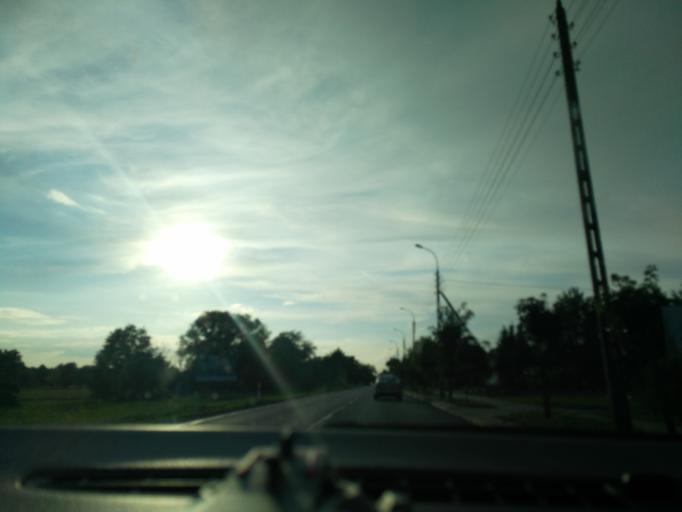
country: PL
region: Lublin Voivodeship
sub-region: Powiat krasnicki
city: Krasnik
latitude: 50.9141
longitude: 22.2477
